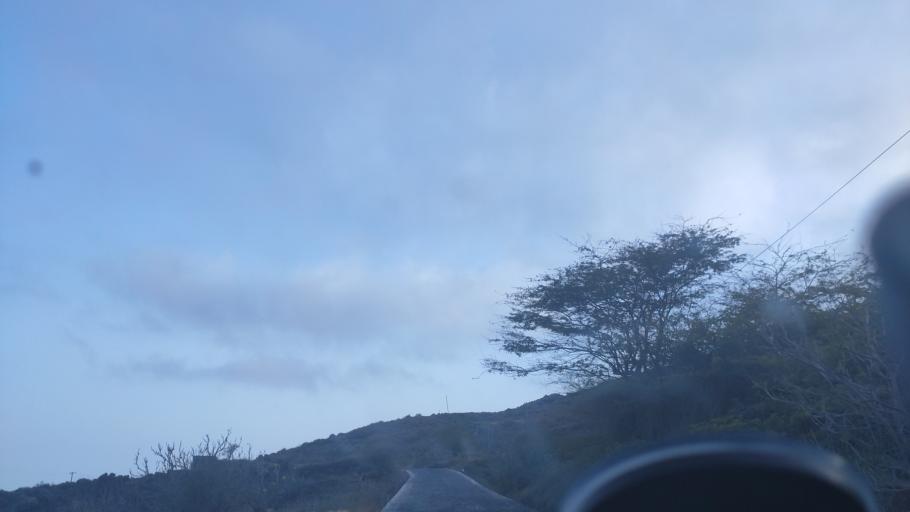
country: CV
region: Mosteiros
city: Porto dos Mosteiros
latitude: 15.0079
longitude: -24.3055
